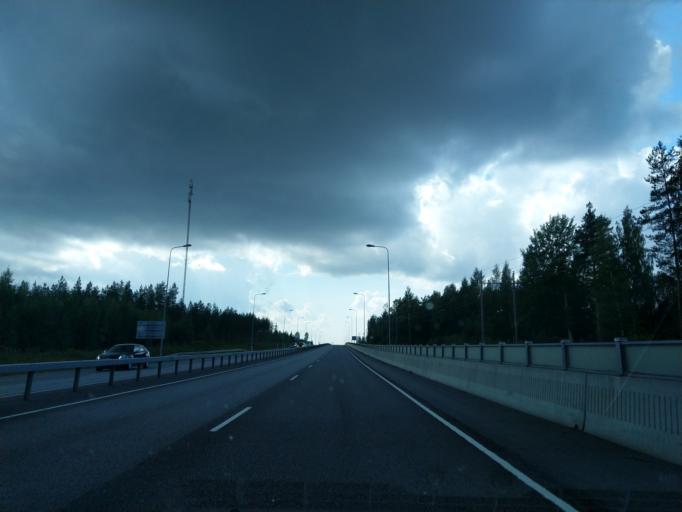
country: FI
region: South Karelia
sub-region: Imatra
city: Imatra
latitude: 61.1646
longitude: 28.6719
